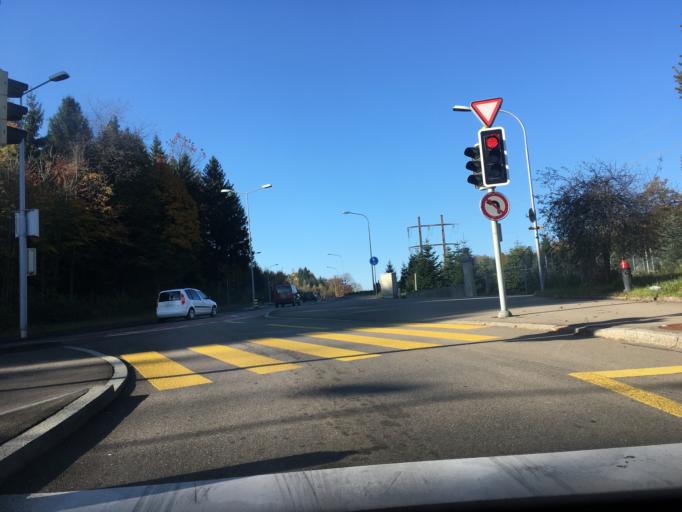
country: CH
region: Zurich
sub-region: Bezirk Dietikon
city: Uitikon
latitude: 47.3708
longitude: 8.4701
